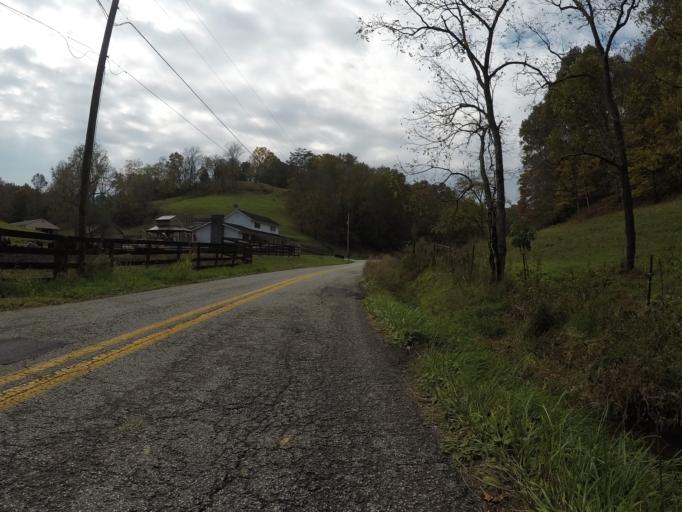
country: US
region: West Virginia
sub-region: Cabell County
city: Huntington
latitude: 38.3708
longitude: -82.4134
